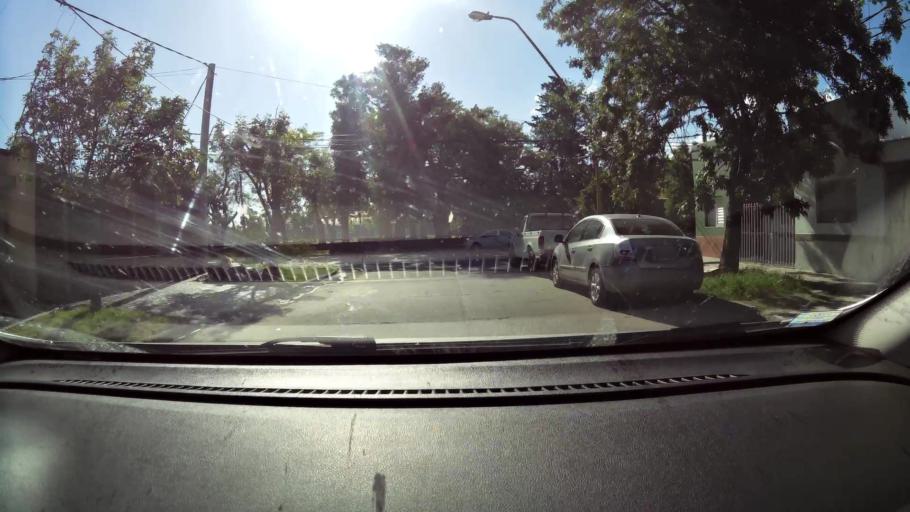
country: AR
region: Santa Fe
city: Santa Fe de la Vera Cruz
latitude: -31.6059
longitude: -60.6855
